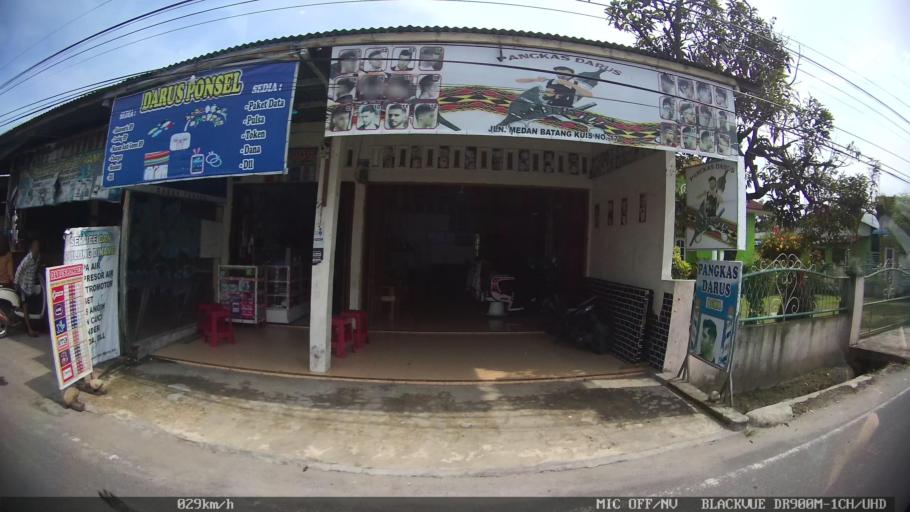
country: ID
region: North Sumatra
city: Percut
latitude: 3.6072
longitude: 98.7940
